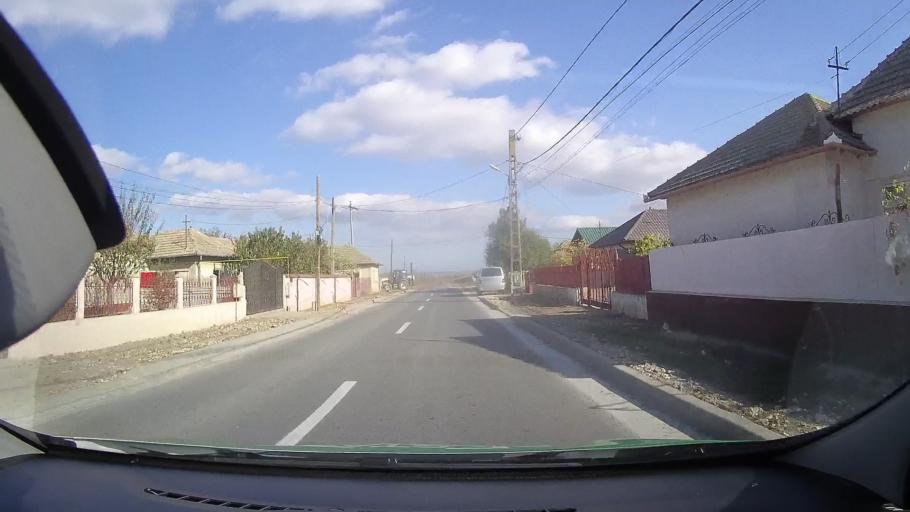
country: RO
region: Constanta
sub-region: Comuna Cogealac
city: Cogealac
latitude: 44.5591
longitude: 28.5710
